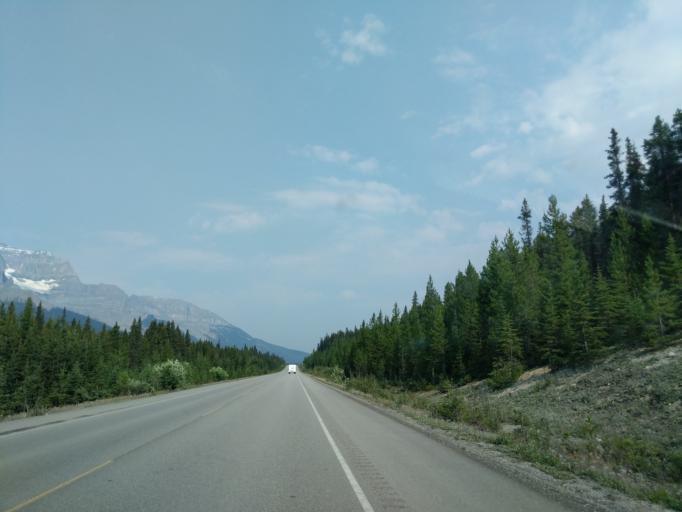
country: CA
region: Alberta
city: Lake Louise
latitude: 51.8657
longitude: -116.6650
